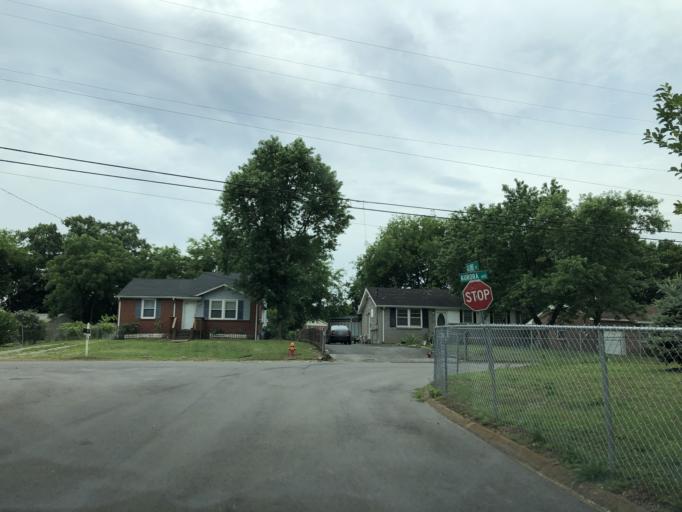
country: US
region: Tennessee
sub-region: Davidson County
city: Goodlettsville
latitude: 36.2843
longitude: -86.7010
